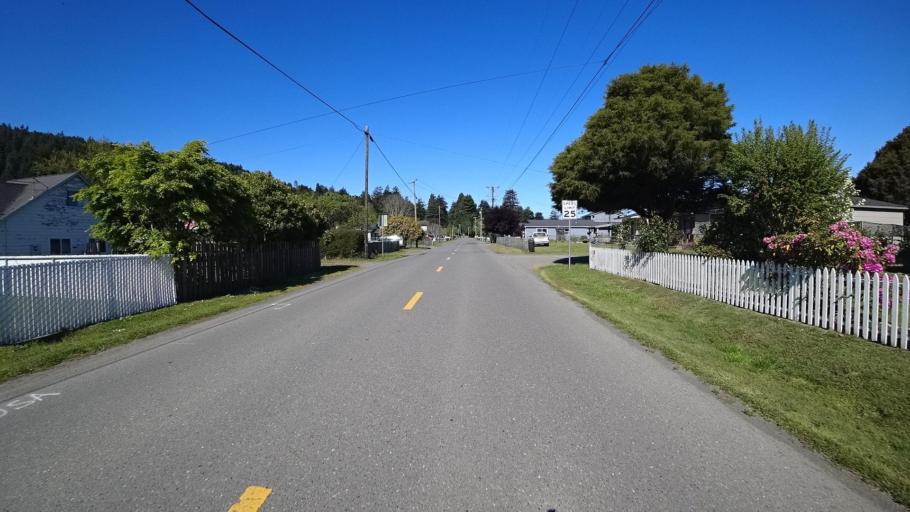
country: US
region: California
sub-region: Humboldt County
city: Rio Dell
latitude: 40.5071
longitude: -124.1202
